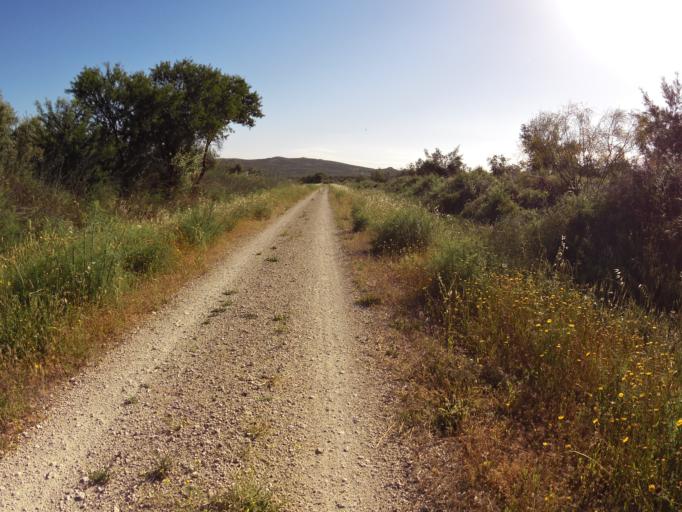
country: ES
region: Andalusia
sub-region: Province of Cordoba
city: Luque
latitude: 37.5753
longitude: -4.2199
